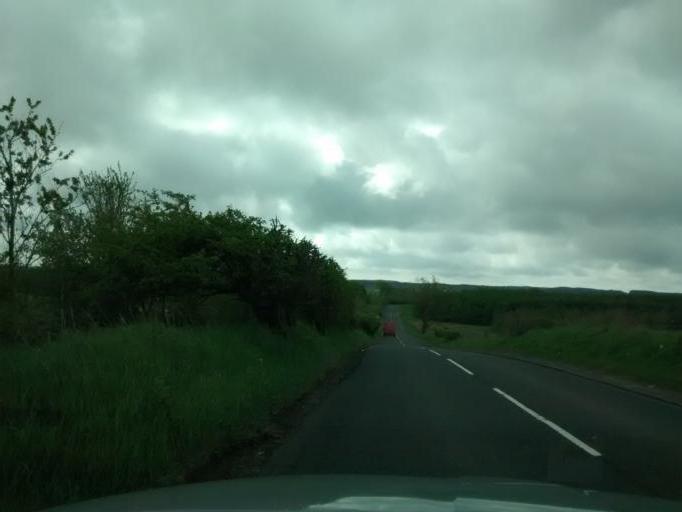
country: GB
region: Scotland
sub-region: North Lanarkshire
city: Harthill
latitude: 55.8719
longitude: -3.7533
